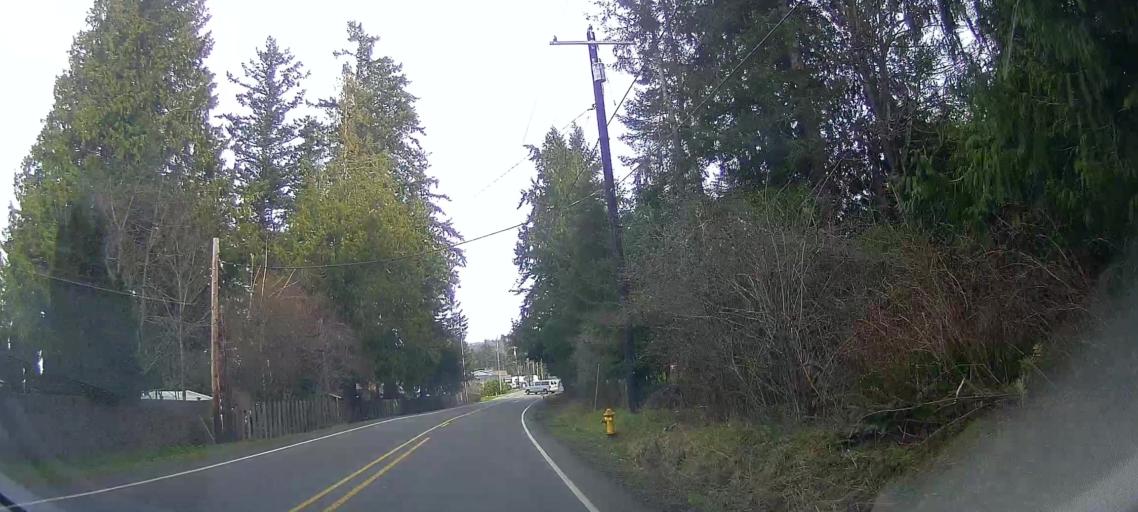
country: US
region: Washington
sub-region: Island County
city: Camano
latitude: 48.2444
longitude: -122.5264
